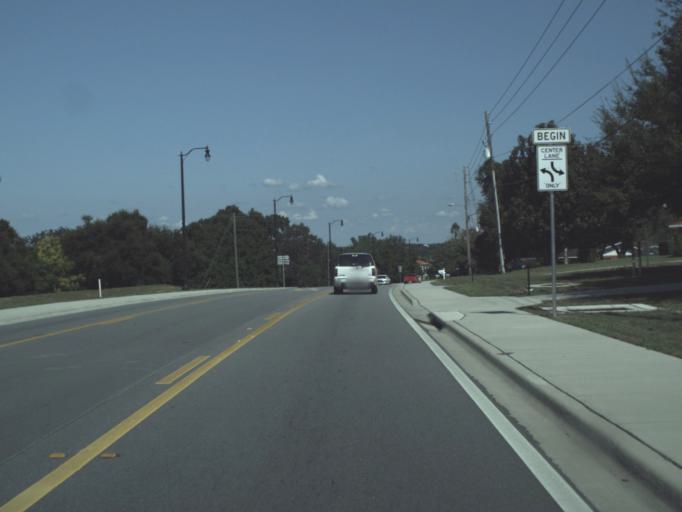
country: US
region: Florida
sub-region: Polk County
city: Haines City
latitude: 28.0859
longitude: -81.6224
